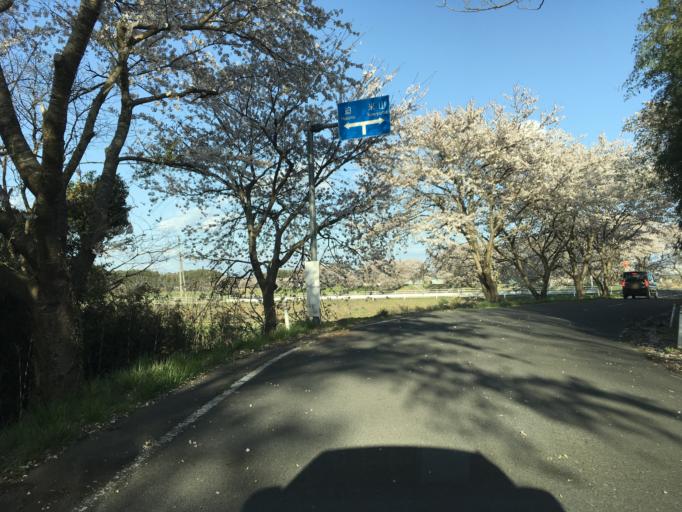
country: JP
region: Miyagi
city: Wakuya
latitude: 38.6421
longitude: 141.1878
